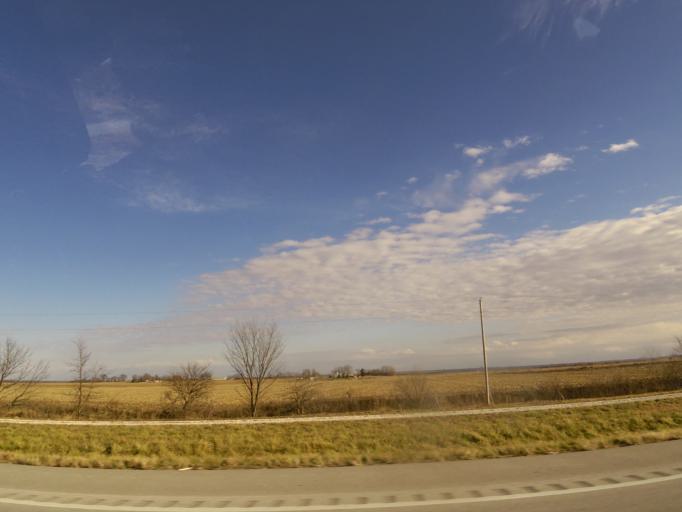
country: US
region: Illinois
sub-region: Adams County
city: Quincy
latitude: 39.9565
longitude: -91.5182
